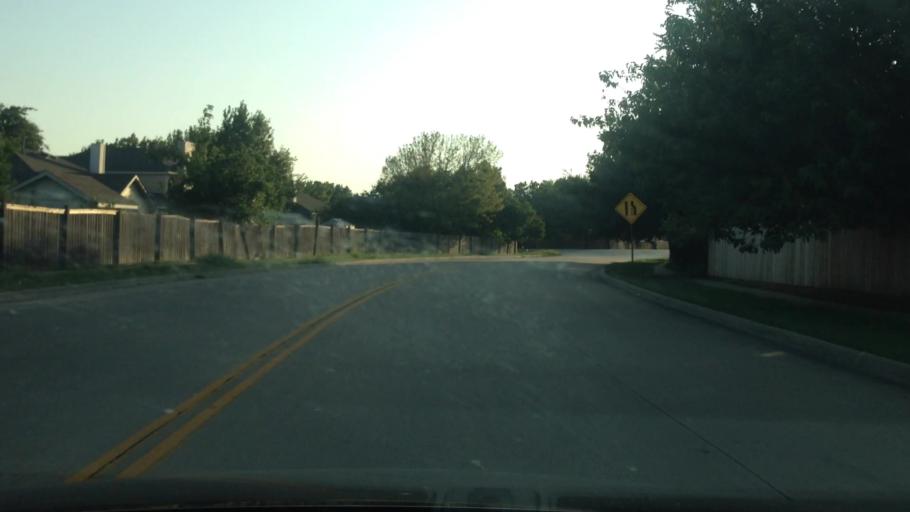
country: US
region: Texas
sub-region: Tarrant County
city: Dalworthington Gardens
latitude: 32.6535
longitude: -97.1008
